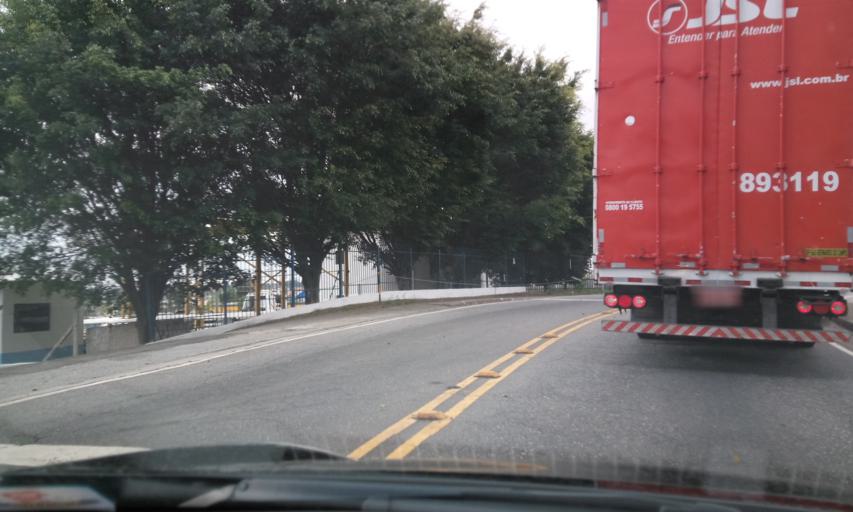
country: BR
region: Sao Paulo
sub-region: Sao Caetano Do Sul
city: Sao Caetano do Sul
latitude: -23.6497
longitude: -46.5825
